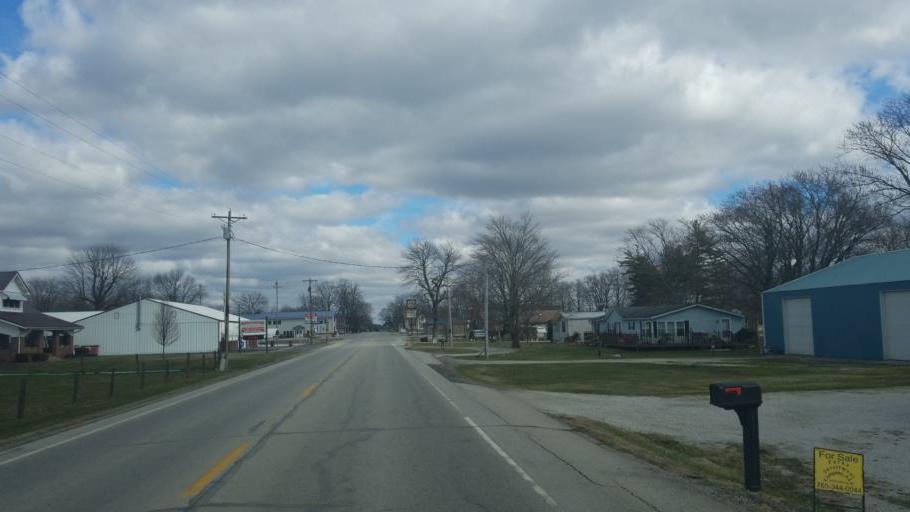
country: US
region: Indiana
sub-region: Parke County
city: Rockville
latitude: 39.7592
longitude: -87.1073
